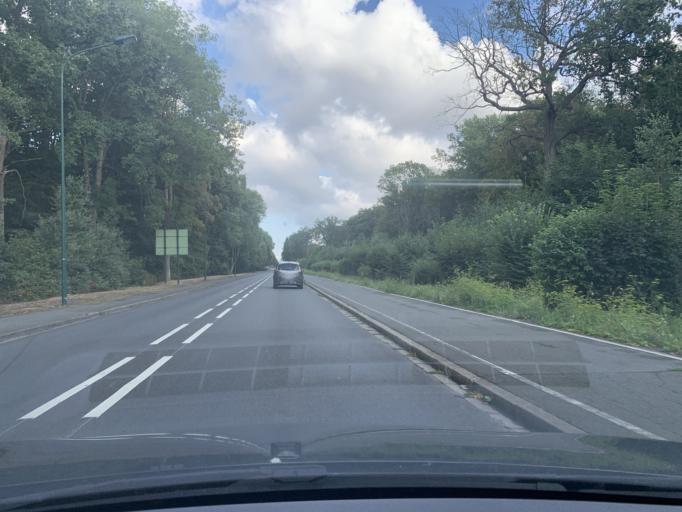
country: FR
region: Nord-Pas-de-Calais
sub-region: Departement du Pas-de-Calais
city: Libercourt
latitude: 50.4878
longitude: 2.9931
